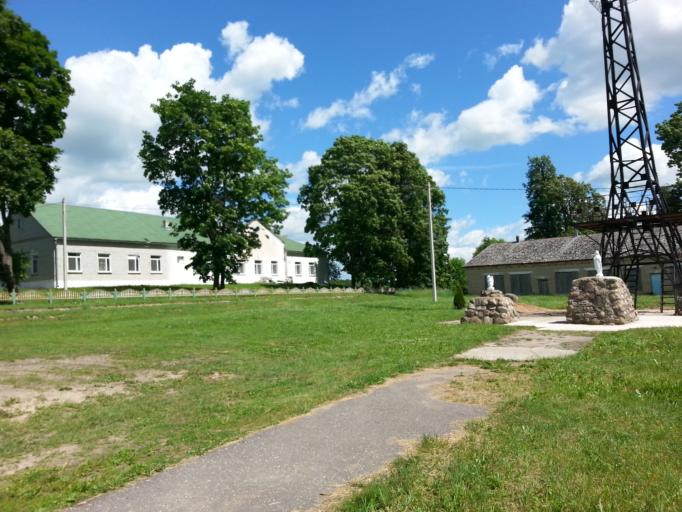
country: BY
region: Vitebsk
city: Mosar
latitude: 55.1561
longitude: 27.3853
